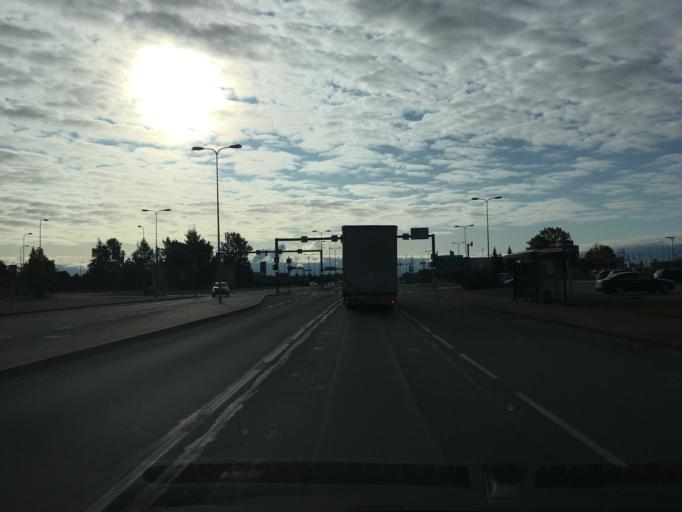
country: EE
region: Harju
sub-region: Tallinna linn
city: Kose
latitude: 59.4308
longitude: 24.8339
